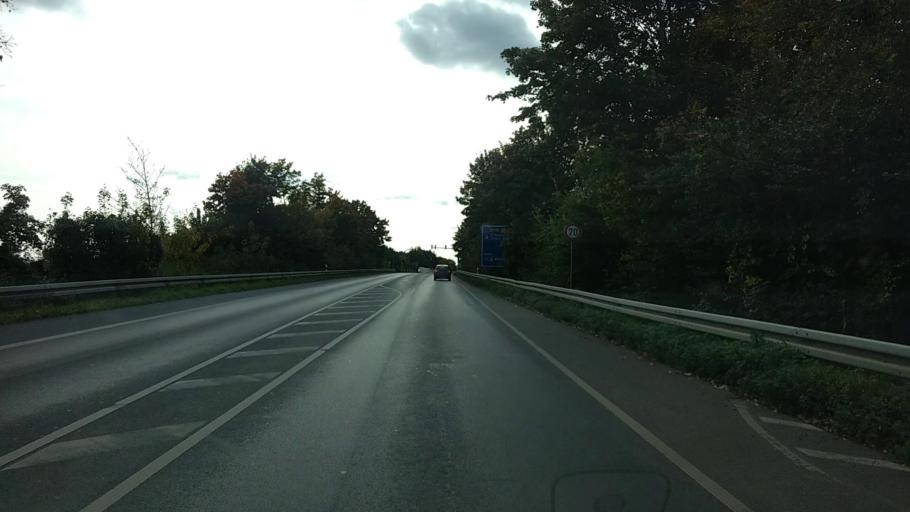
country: DE
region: North Rhine-Westphalia
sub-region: Regierungsbezirk Koln
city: Bergheim
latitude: 50.9397
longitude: 6.6518
